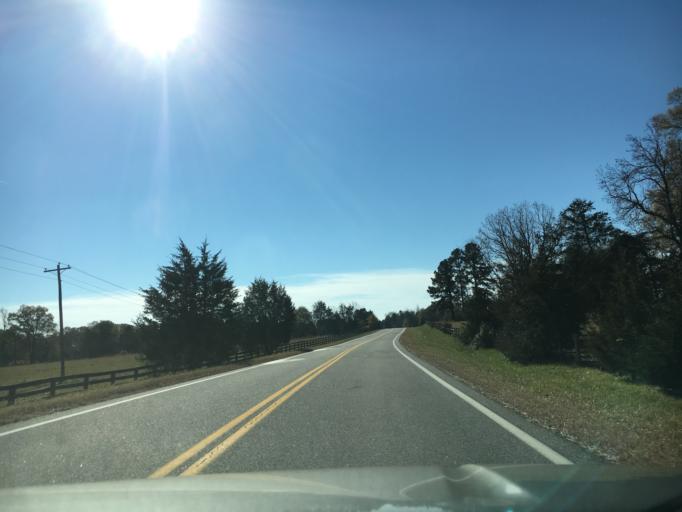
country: US
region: Virginia
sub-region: Cumberland County
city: Cumberland
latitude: 37.5897
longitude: -78.1738
